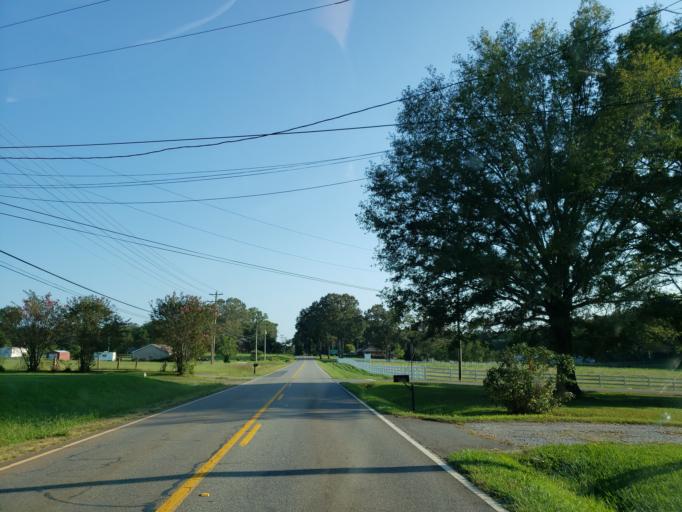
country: US
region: Georgia
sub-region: Murray County
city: Chatsworth
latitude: 34.7797
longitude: -84.8243
